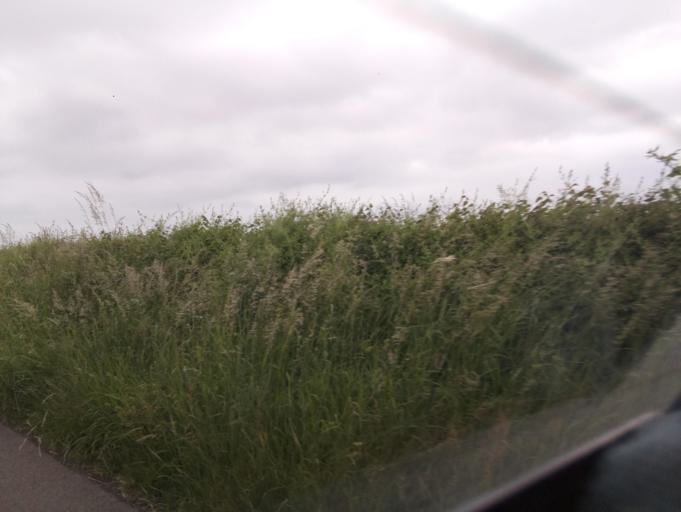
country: GB
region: England
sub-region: Leicestershire
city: Melton Mowbray
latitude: 52.7099
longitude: -0.8328
